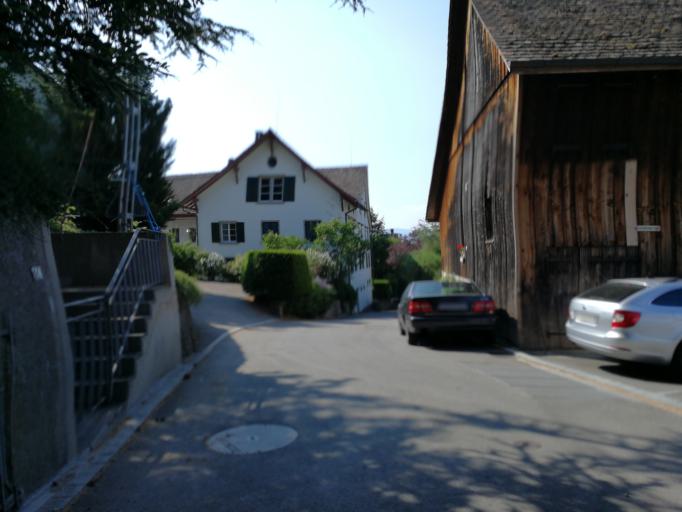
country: CH
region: Zurich
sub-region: Bezirk Meilen
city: Herrliberg
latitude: 47.2878
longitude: 8.6179
